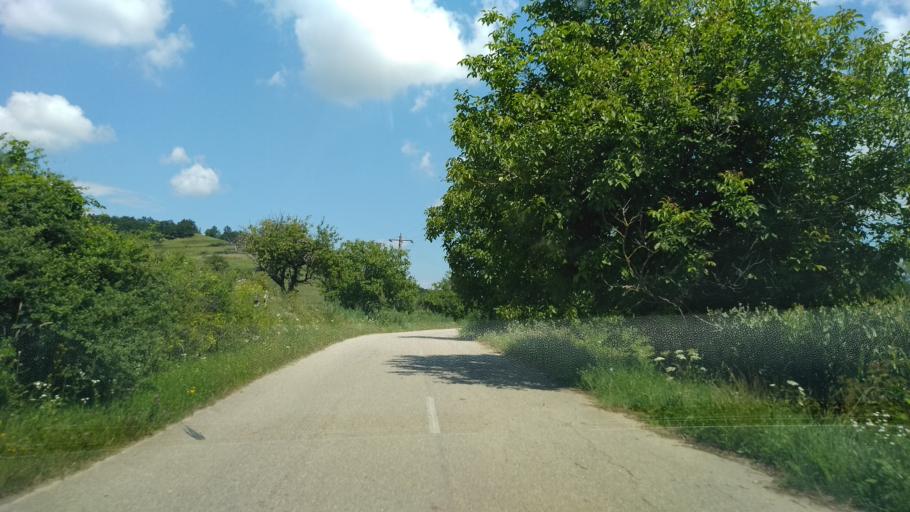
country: RO
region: Hunedoara
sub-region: Comuna Bosorod
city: Bosorod
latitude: 45.7076
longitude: 23.1089
